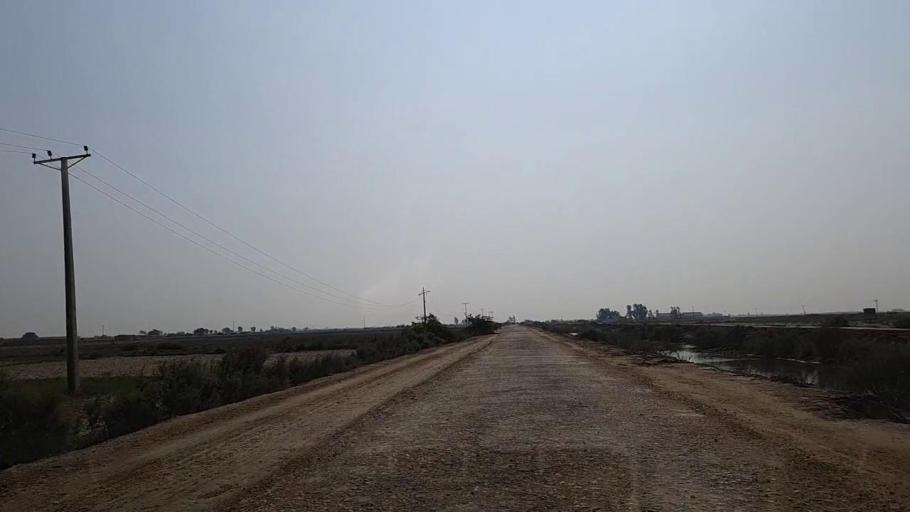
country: PK
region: Sindh
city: Thatta
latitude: 24.7153
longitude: 67.7684
